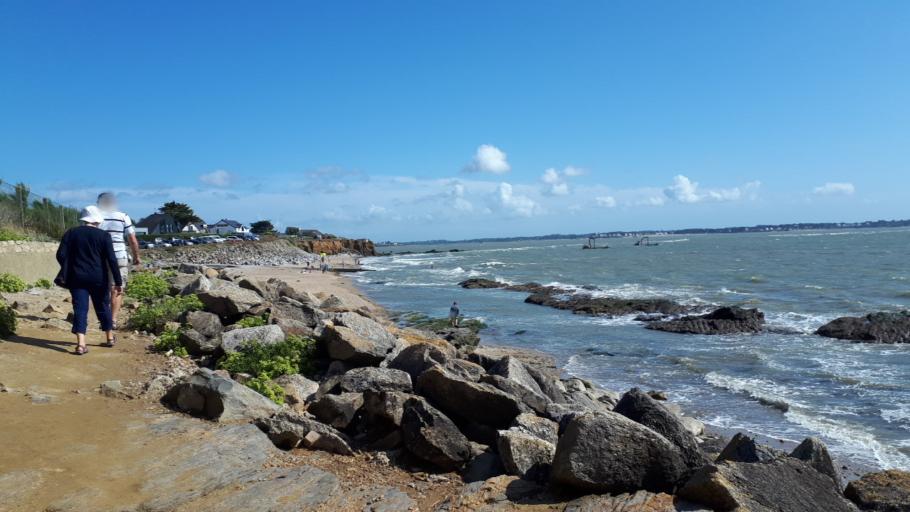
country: FR
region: Brittany
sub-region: Departement du Morbihan
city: Penestin
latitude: 47.4441
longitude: -2.4843
